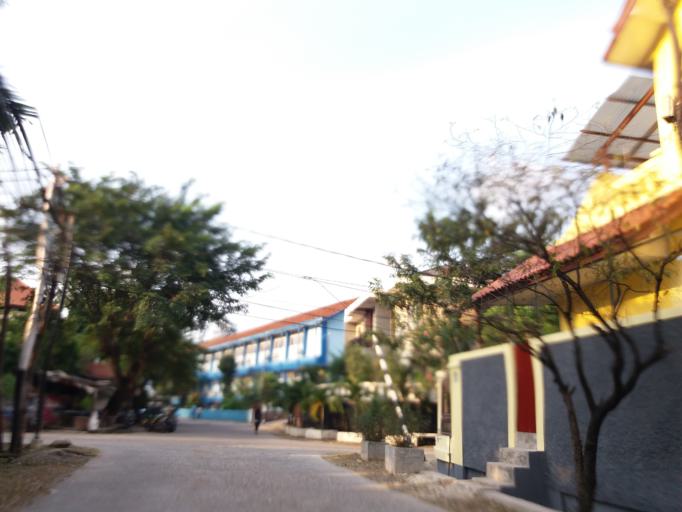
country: ID
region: Jakarta Raya
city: Jakarta
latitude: -6.2404
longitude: 106.8160
